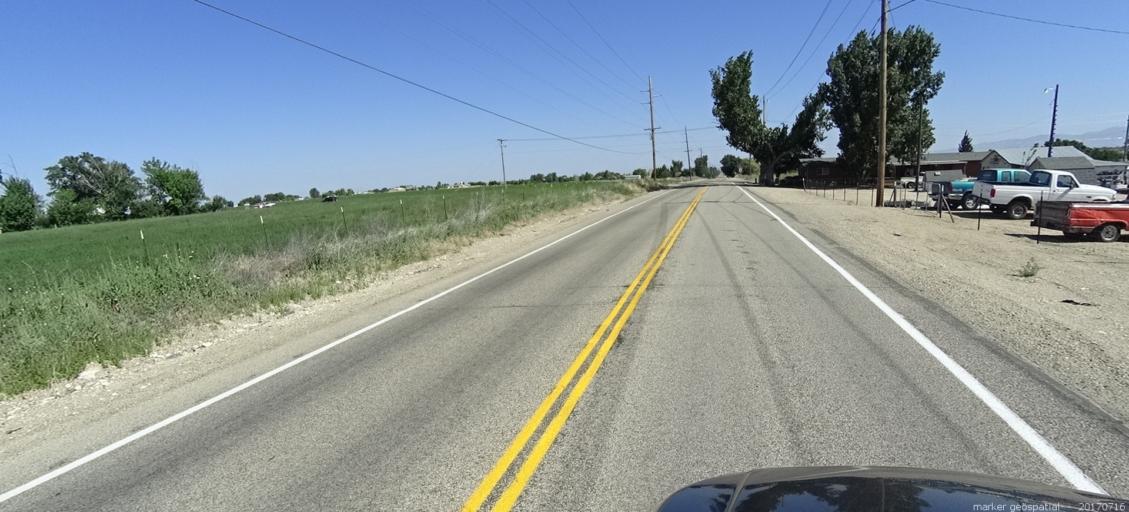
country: US
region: Idaho
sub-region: Ada County
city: Kuna
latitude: 43.5162
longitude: -116.3345
